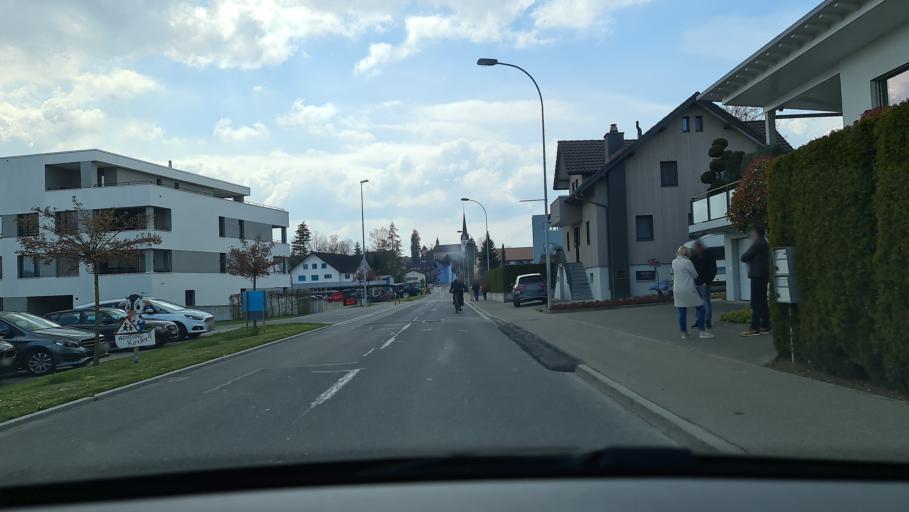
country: CH
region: Lucerne
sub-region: Hochdorf District
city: Ballwil
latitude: 47.1540
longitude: 8.3275
